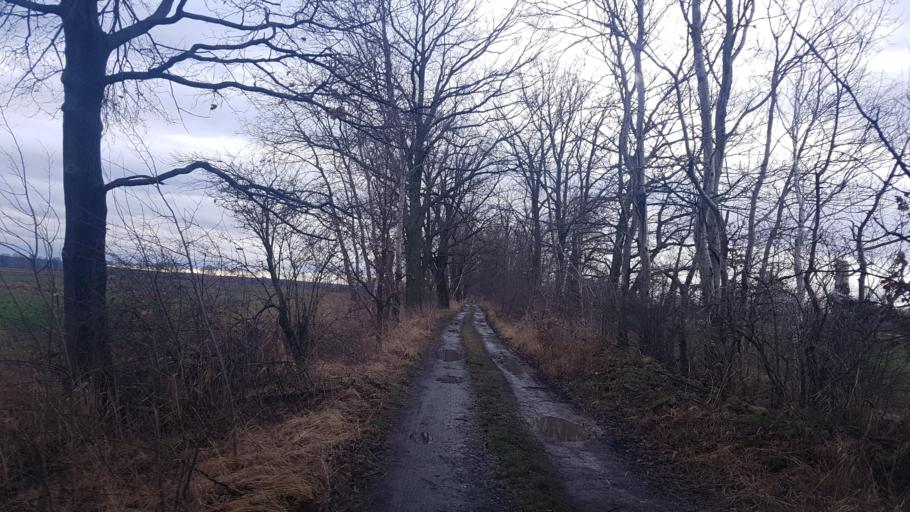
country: DE
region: Brandenburg
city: Plessa
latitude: 51.4347
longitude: 13.6500
